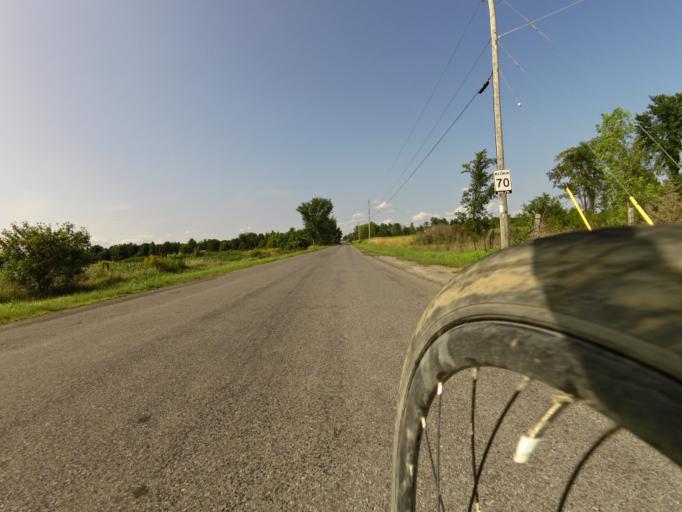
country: CA
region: Ontario
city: Kingston
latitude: 44.3109
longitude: -76.6714
